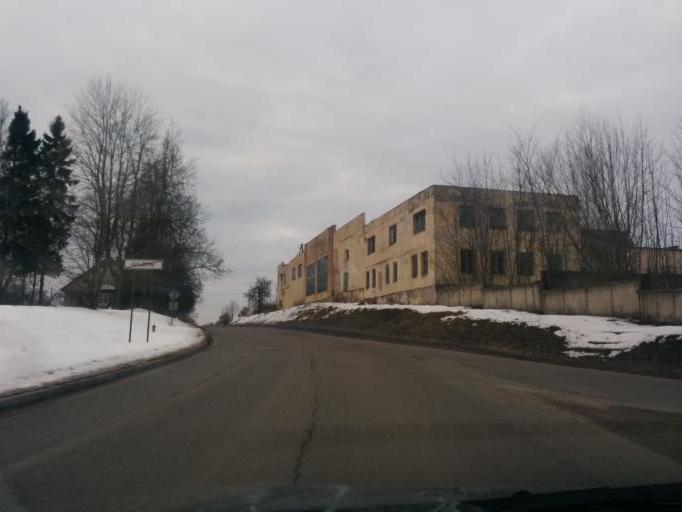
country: LV
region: Gulbenes Rajons
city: Gulbene
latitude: 57.1841
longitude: 26.7366
